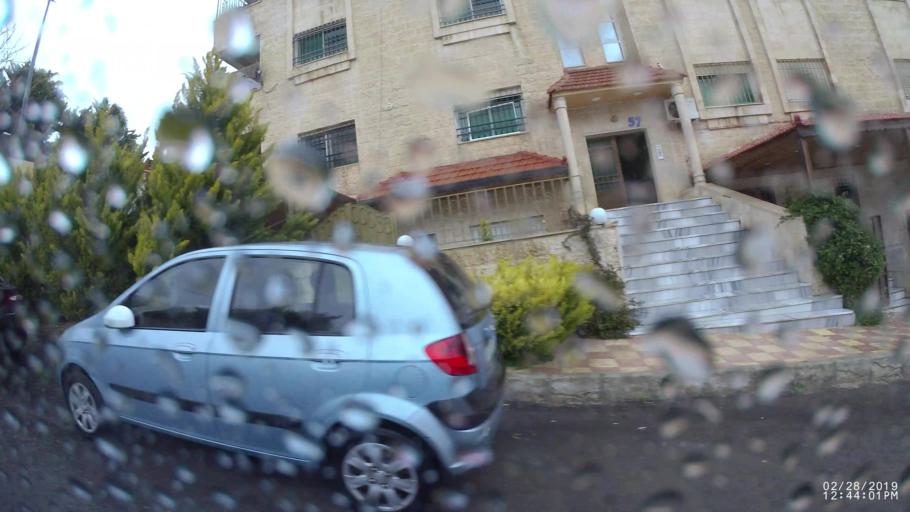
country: JO
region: Amman
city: Al Jubayhah
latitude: 32.0298
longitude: 35.8836
